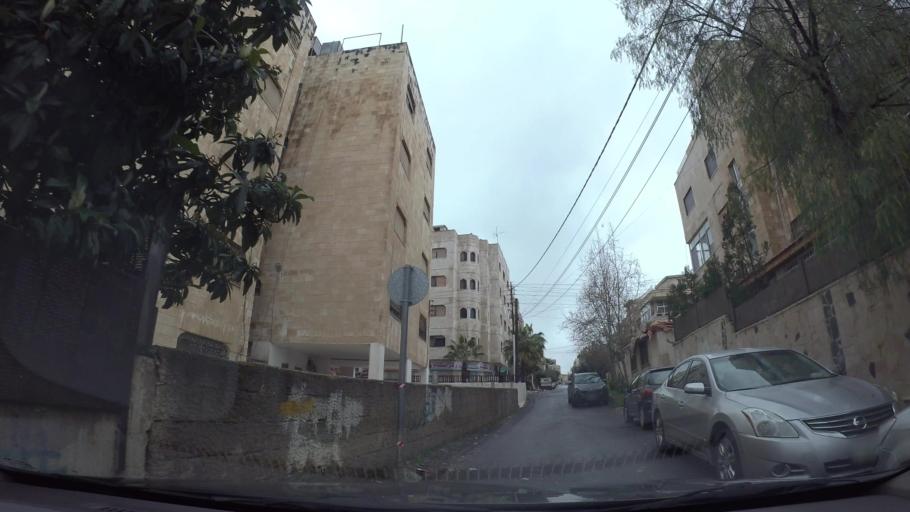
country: JO
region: Amman
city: Wadi as Sir
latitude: 31.9654
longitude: 35.8598
